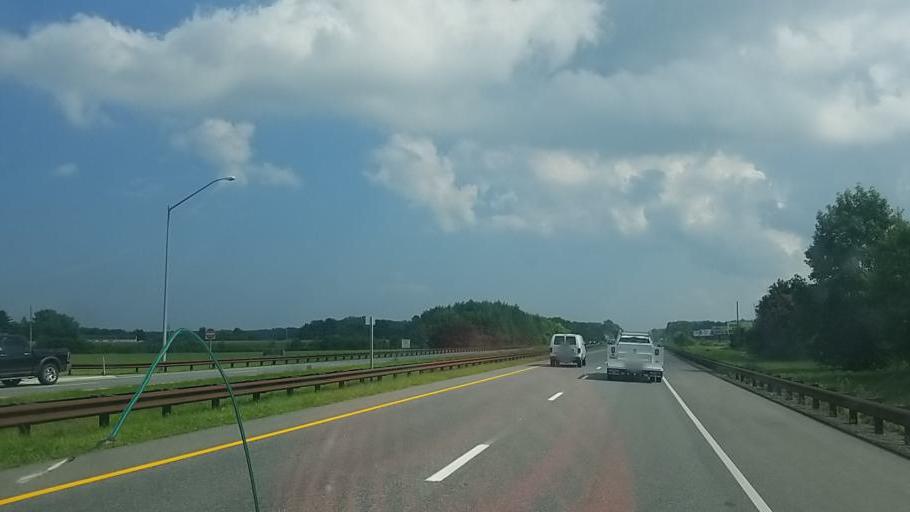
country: US
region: Delaware
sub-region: Sussex County
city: Selbyville
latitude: 38.4336
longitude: -75.2226
